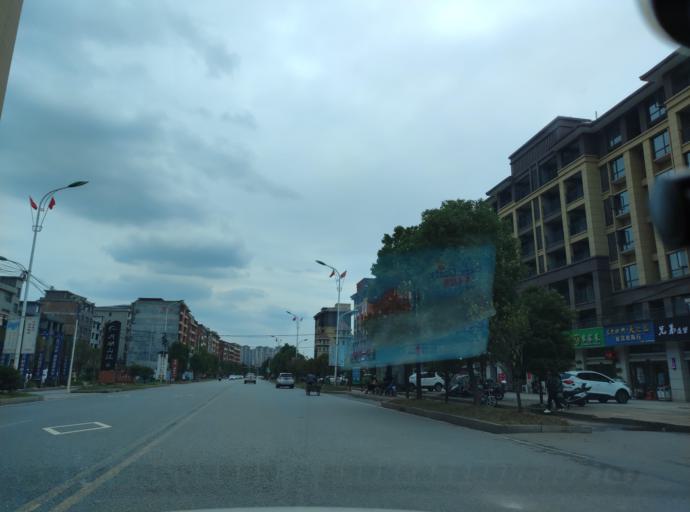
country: CN
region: Jiangxi Sheng
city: Pingxiang
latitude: 27.6762
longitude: 113.9062
